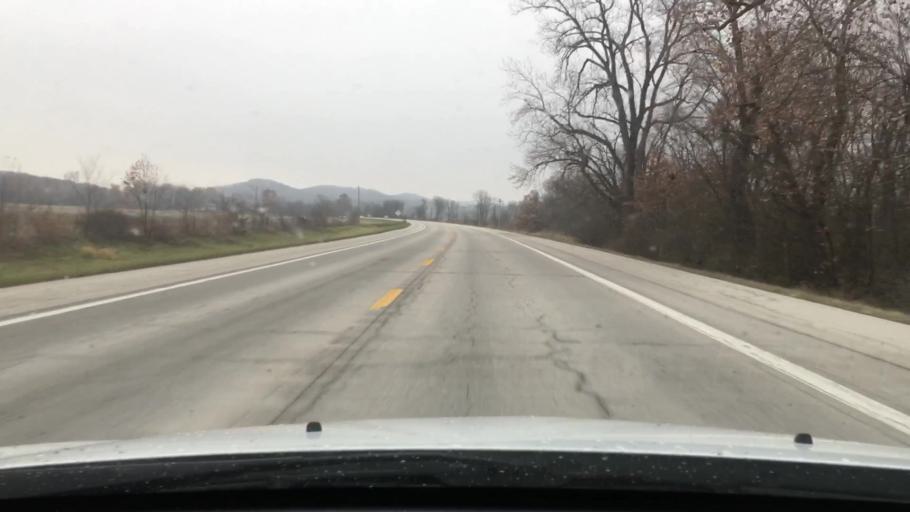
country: US
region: Missouri
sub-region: Pike County
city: Bowling Green
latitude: 39.3856
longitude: -91.1239
